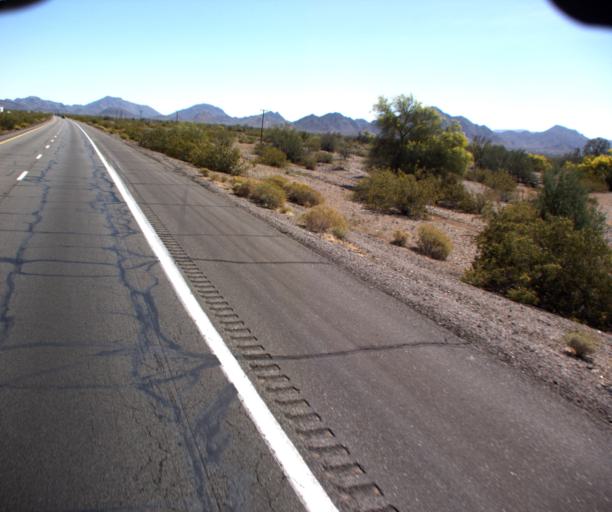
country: US
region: Arizona
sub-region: La Paz County
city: Quartzsite
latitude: 33.6697
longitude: -114.1615
